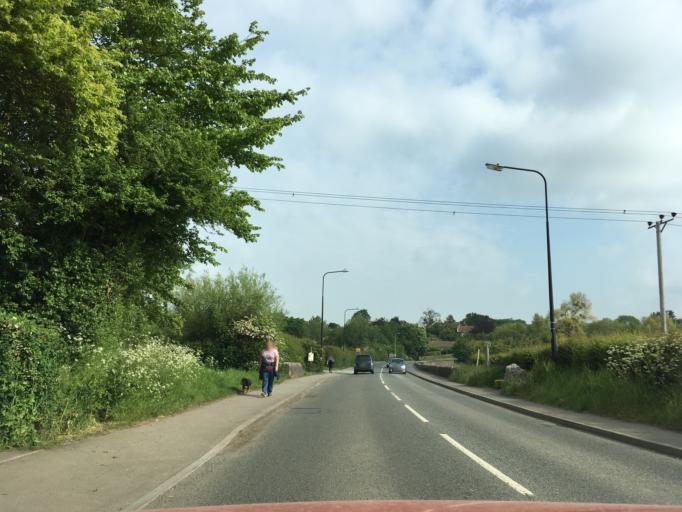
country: GB
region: England
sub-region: North Somerset
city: Nailsea
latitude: 51.4209
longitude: -2.7510
